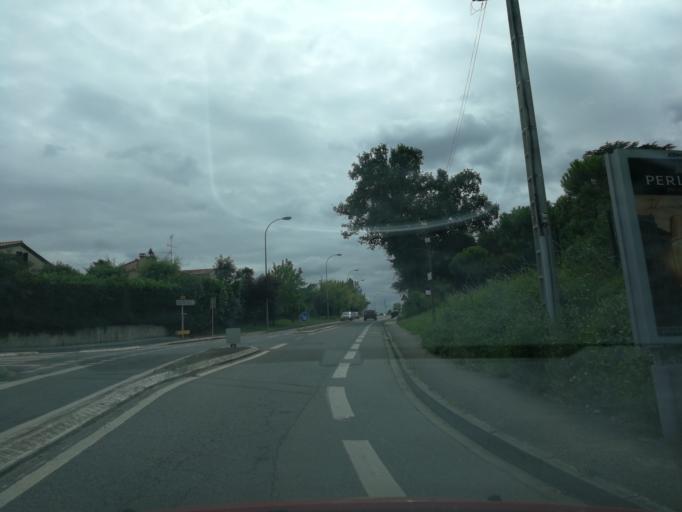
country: FR
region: Midi-Pyrenees
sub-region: Departement de la Haute-Garonne
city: Ramonville-Saint-Agne
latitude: 43.5363
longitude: 1.4724
